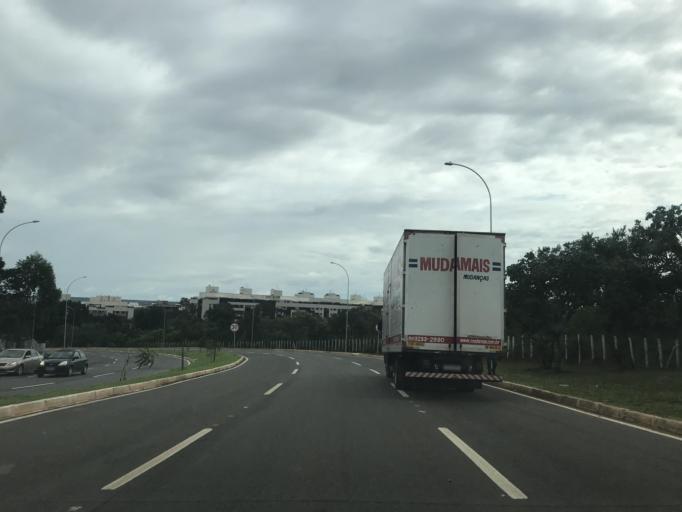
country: BR
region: Federal District
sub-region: Brasilia
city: Brasilia
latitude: -15.7509
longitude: -47.9141
